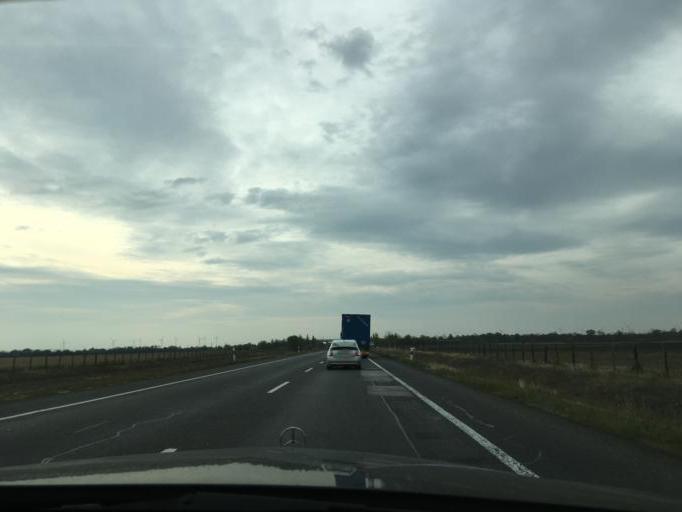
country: HU
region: Gyor-Moson-Sopron
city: Rajka
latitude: 47.9187
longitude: 17.1777
